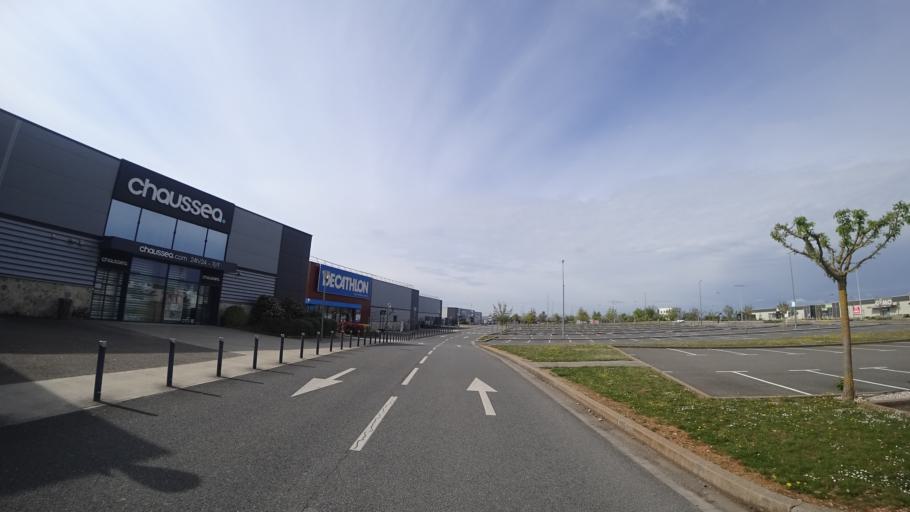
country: FR
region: Midi-Pyrenees
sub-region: Departement de l'Aveyron
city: Sebazac-Concoures
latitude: 44.3963
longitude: 2.6059
